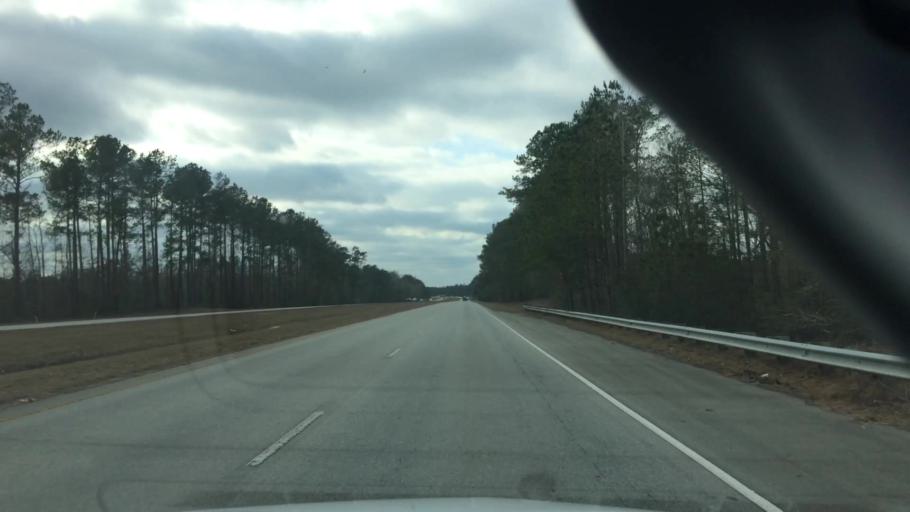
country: US
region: North Carolina
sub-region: Brunswick County
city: Bolivia
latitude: 34.0661
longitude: -78.1864
